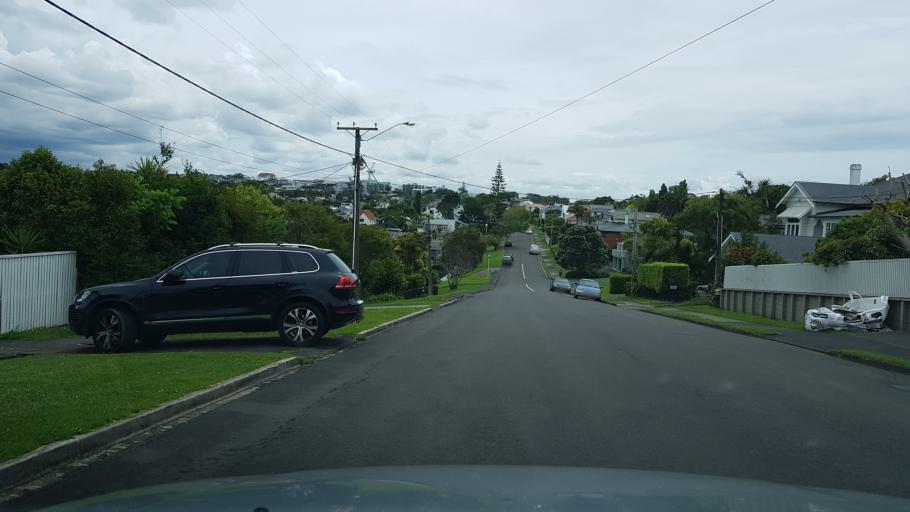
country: NZ
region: Auckland
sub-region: Auckland
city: North Shore
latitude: -36.8194
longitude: 174.7321
